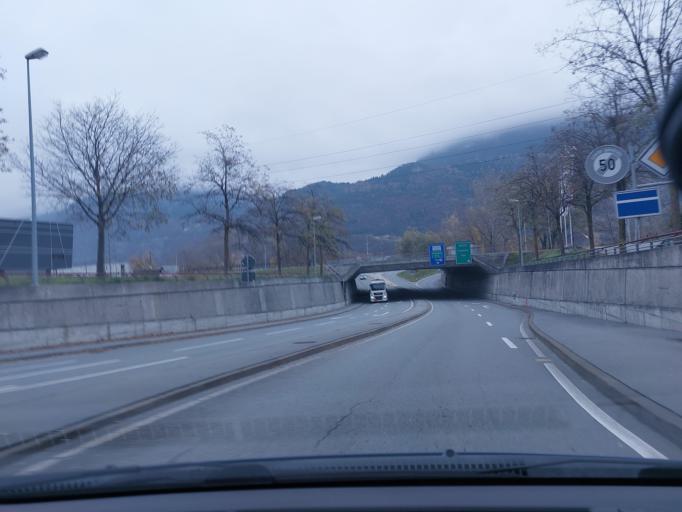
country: CH
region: Valais
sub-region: Sierre District
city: Chalais
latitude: 46.2811
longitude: 7.5109
